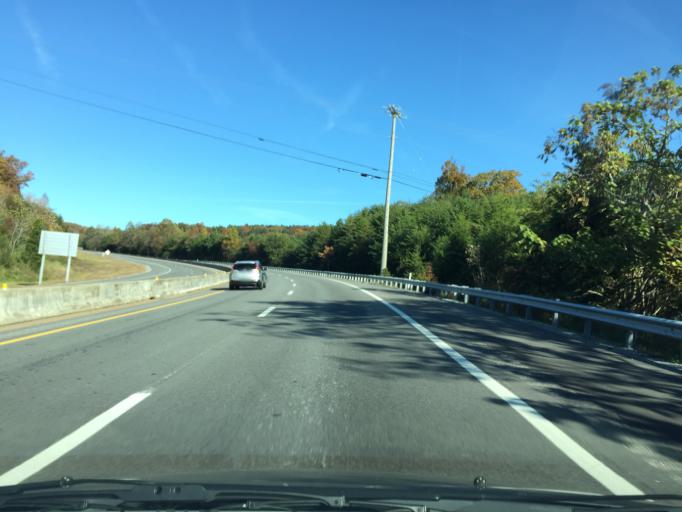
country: US
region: Tennessee
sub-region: Hamilton County
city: Sale Creek
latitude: 35.3230
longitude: -85.1603
